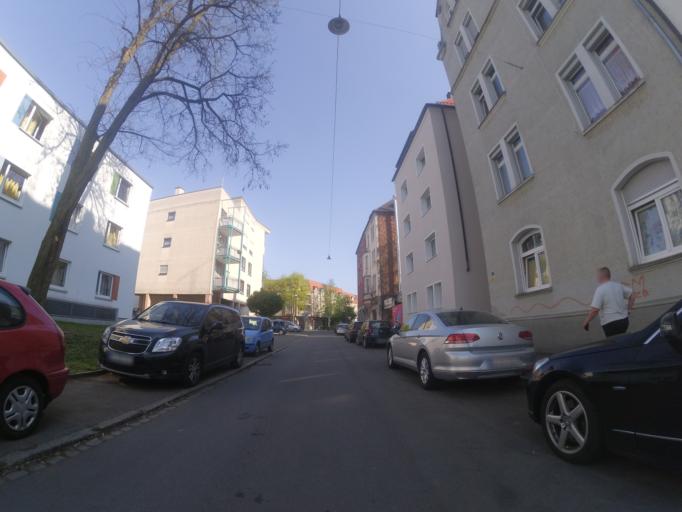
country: DE
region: Baden-Wuerttemberg
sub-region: Tuebingen Region
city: Ulm
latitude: 48.4049
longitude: 10.0012
